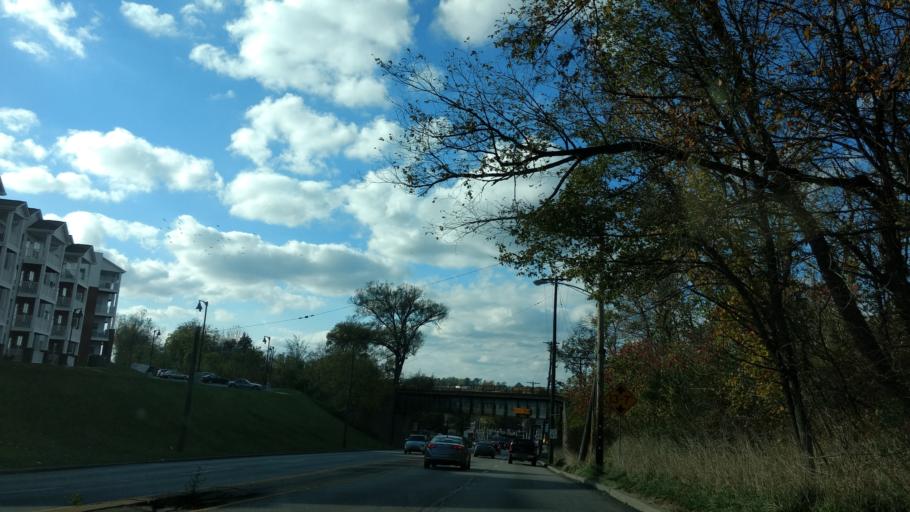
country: US
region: Pennsylvania
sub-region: Allegheny County
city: Pleasant Hills
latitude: 40.3422
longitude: -79.9667
